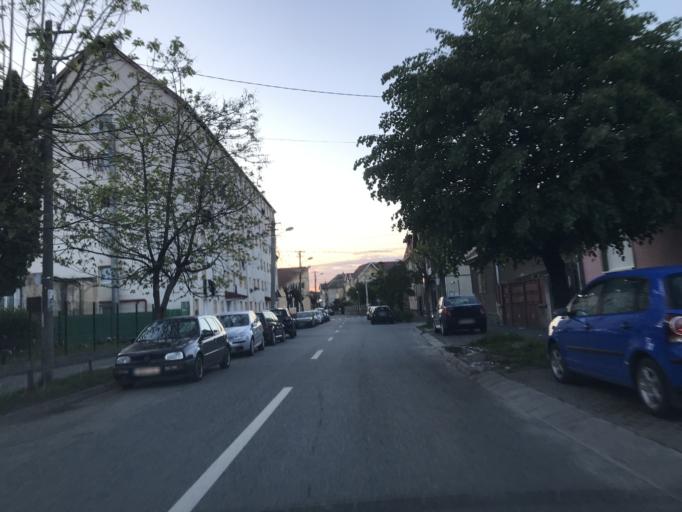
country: RO
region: Sibiu
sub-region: Municipiul Sibiu
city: Sibiu
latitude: 45.8018
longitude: 24.1661
